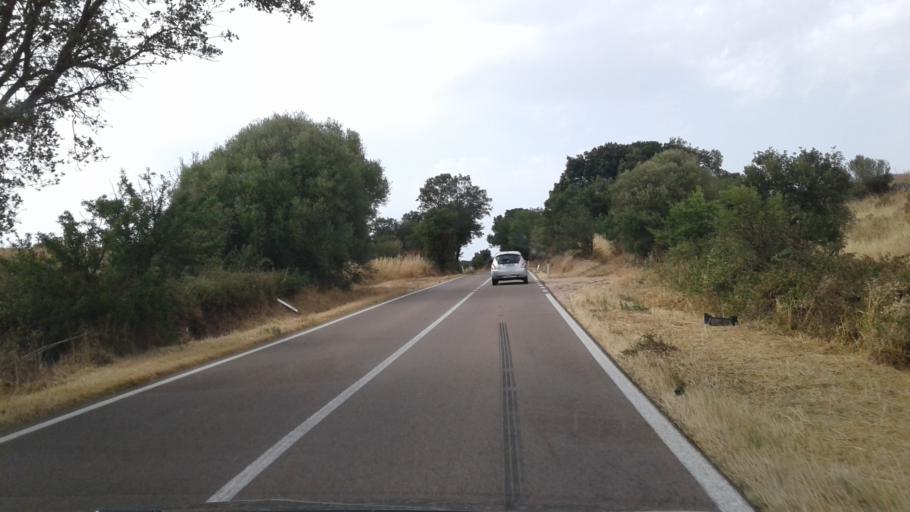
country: IT
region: Sardinia
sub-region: Provincia di Olbia-Tempio
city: Sant'Antonio di Gallura
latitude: 40.9476
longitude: 9.2977
